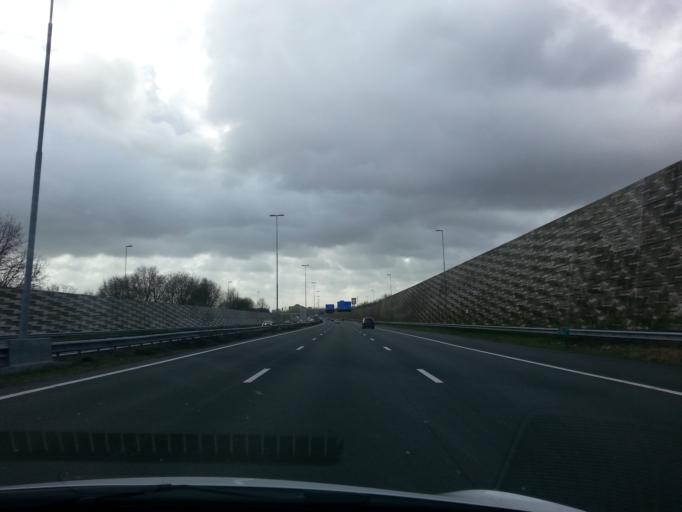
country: NL
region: North Brabant
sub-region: Gemeente 's-Hertogenbosch
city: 's-Hertogenbosch
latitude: 51.7347
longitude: 5.3088
